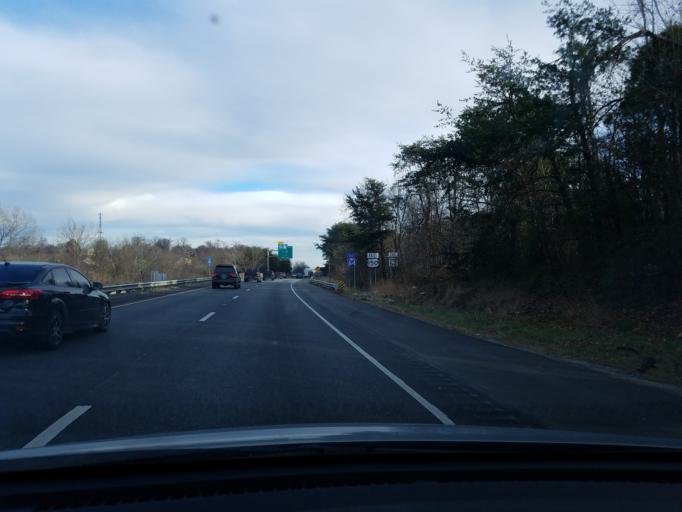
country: US
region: Indiana
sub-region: Floyd County
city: New Albany
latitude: 38.3038
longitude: -85.8802
